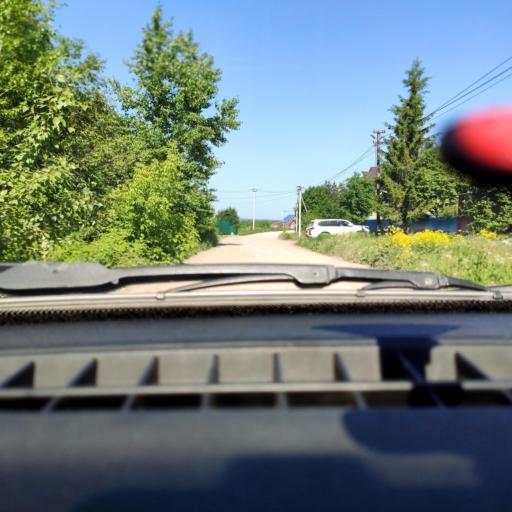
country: RU
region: Bashkortostan
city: Ufa
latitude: 54.6072
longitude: 55.9510
